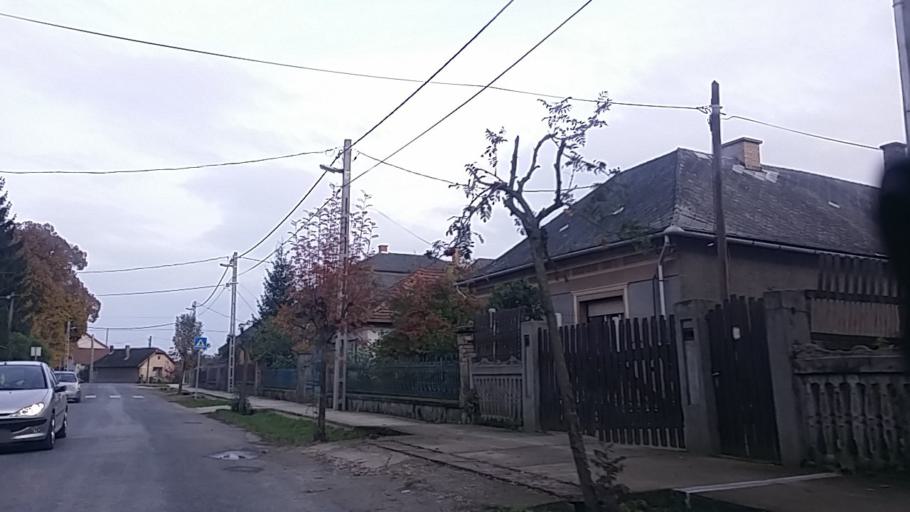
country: HU
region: Borsod-Abauj-Zemplen
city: Putnok
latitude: 48.2739
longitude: 20.4605
